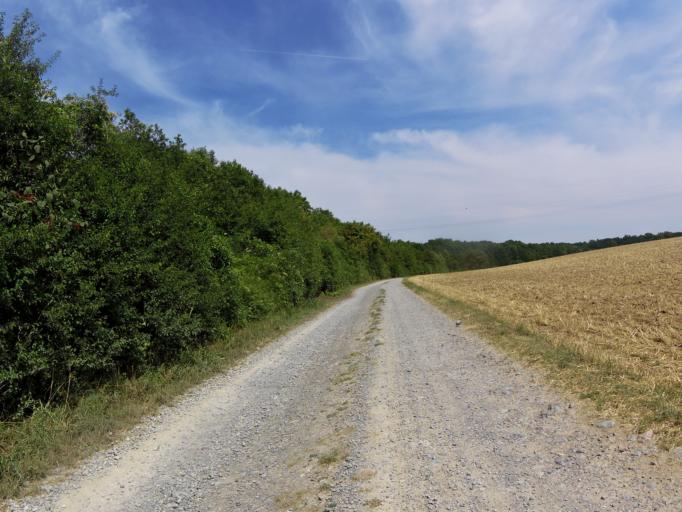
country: DE
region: Bavaria
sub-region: Regierungsbezirk Unterfranken
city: Gerbrunn
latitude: 49.7941
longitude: 10.0072
